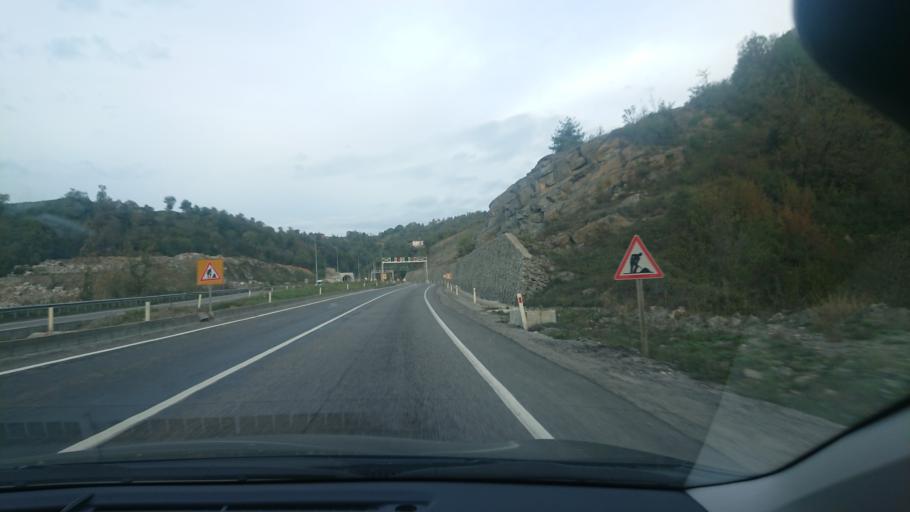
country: TR
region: Zonguldak
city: Beycuma
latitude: 41.4104
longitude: 31.9277
